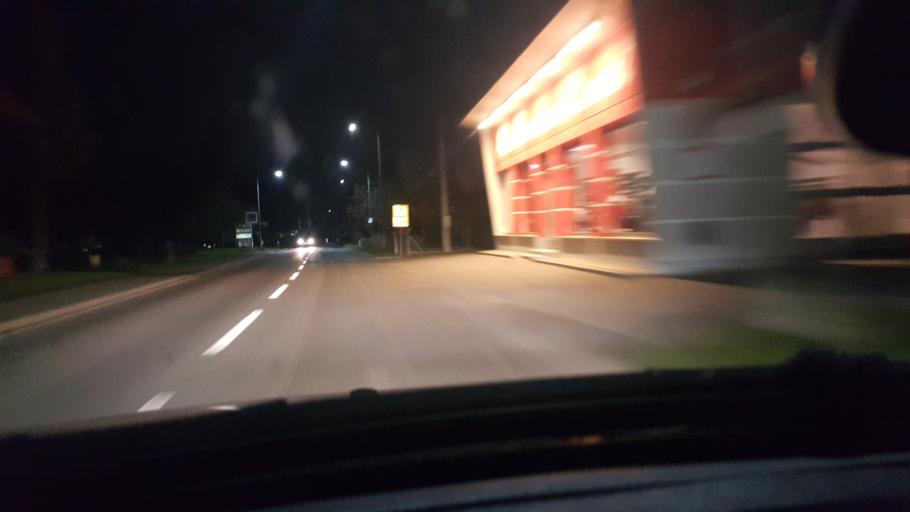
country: AT
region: Styria
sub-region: Politischer Bezirk Deutschlandsberg
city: Sankt Martin im Sulmtal
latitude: 46.7555
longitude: 15.2979
